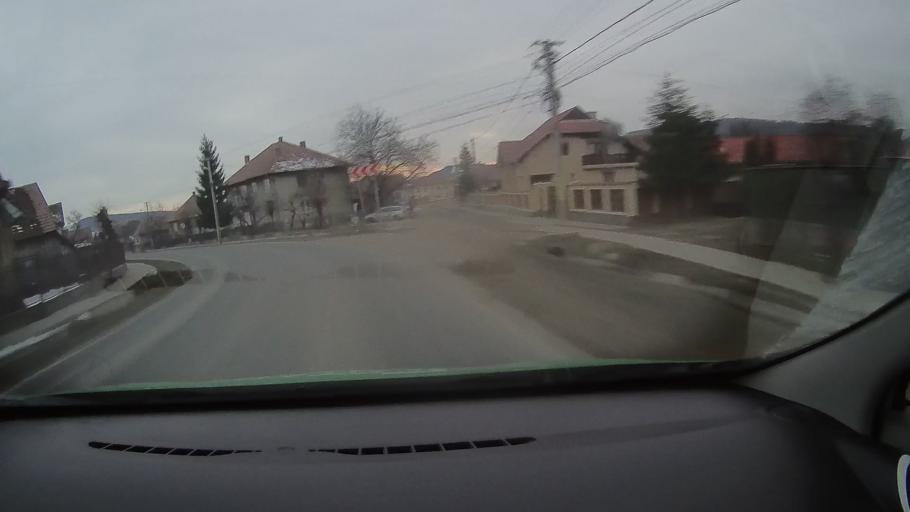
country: RO
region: Harghita
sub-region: Comuna Feliceni
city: Feliceni
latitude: 46.2737
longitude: 25.2779
